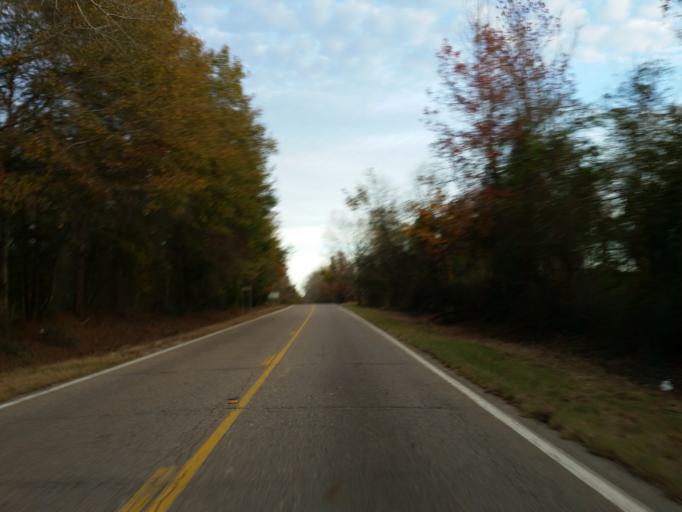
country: US
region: Alabama
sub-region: Sumter County
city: York
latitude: 32.4240
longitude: -88.4352
